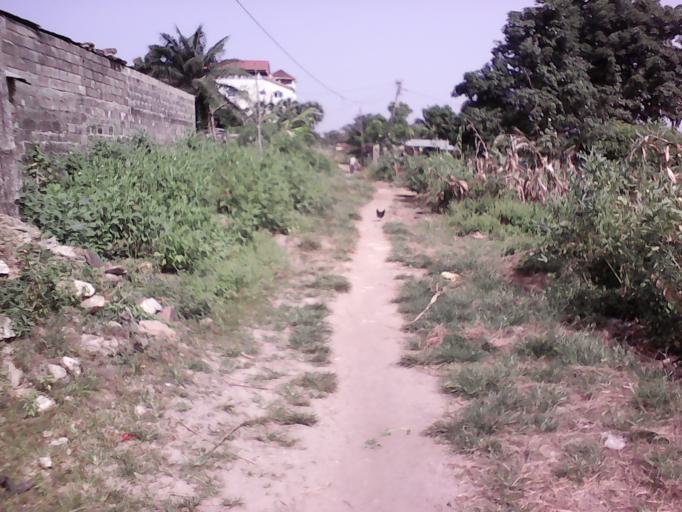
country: TG
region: Kara
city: Kara
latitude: 9.5562
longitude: 1.1948
